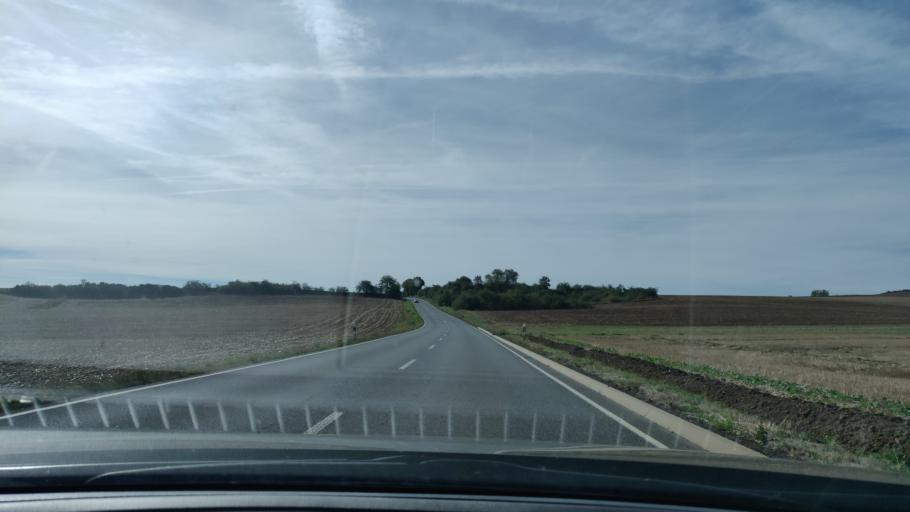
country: DE
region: Hesse
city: Fritzlar
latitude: 51.1518
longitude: 9.2739
